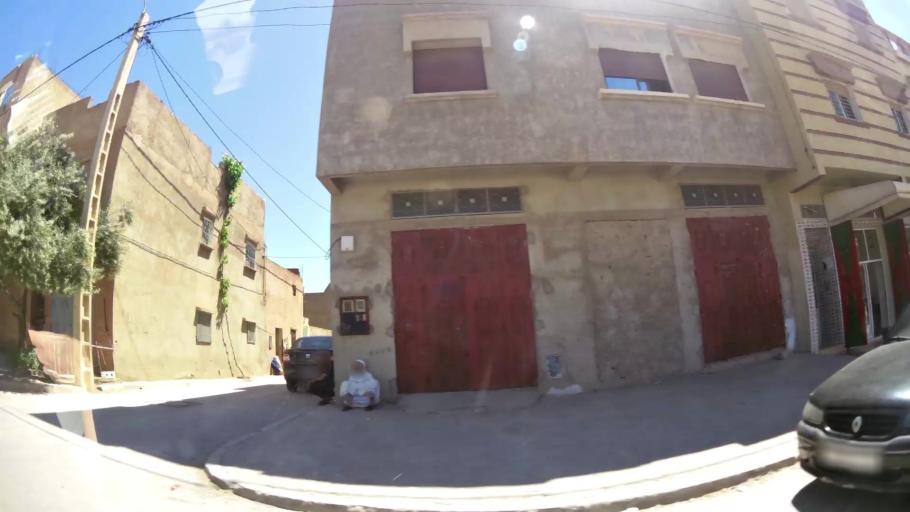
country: MA
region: Oriental
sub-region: Oujda-Angad
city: Oujda
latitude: 34.6629
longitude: -1.8813
